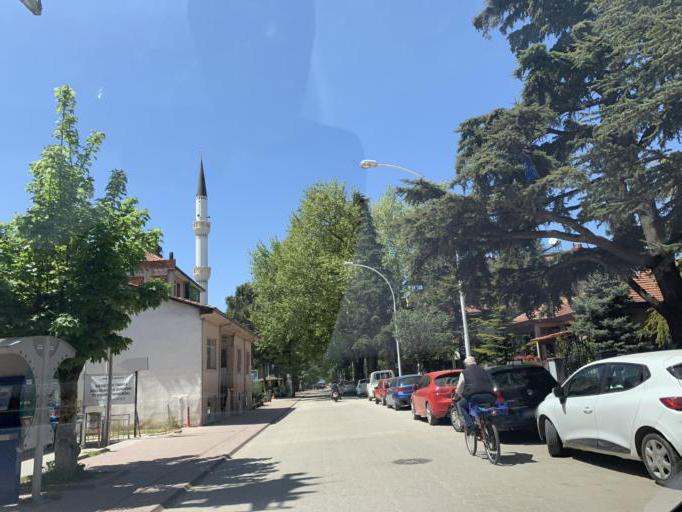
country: TR
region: Bursa
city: Iznik
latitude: 40.4296
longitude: 29.7179
